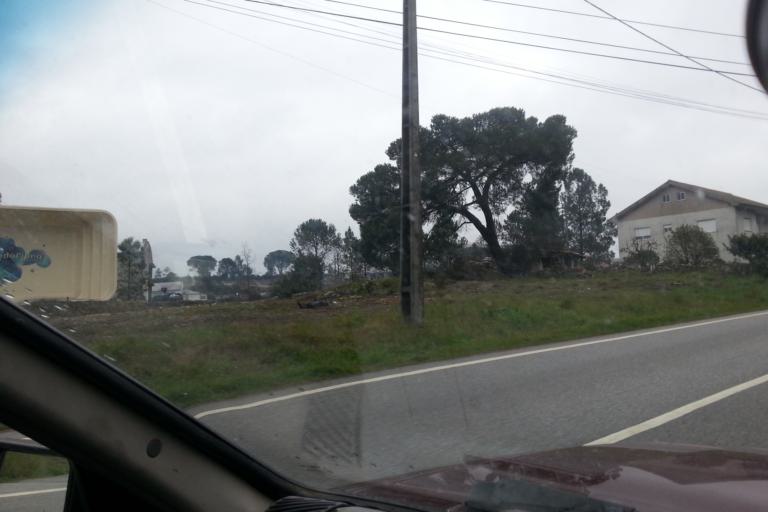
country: PT
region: Viseu
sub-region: Mangualde
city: Mangualde
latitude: 40.6017
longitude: -7.7894
